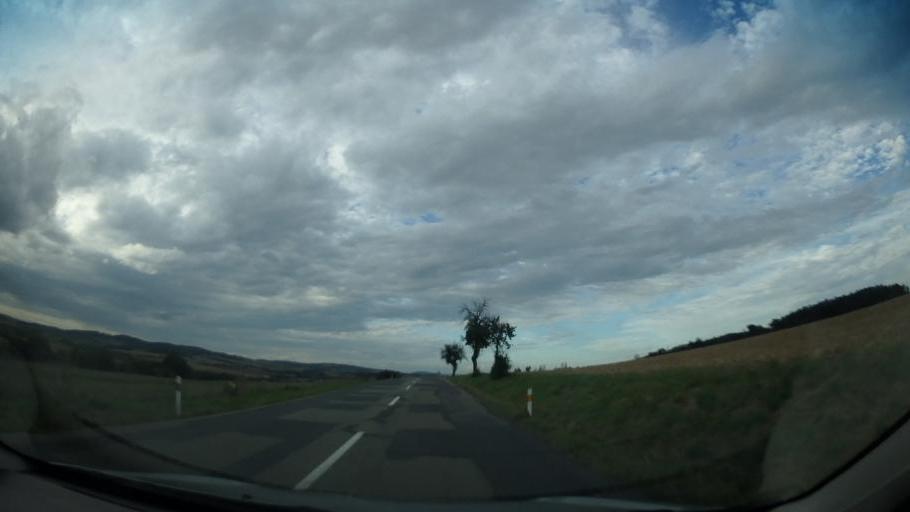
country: CZ
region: South Moravian
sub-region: Okres Blansko
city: Boskovice
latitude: 49.5033
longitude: 16.6694
